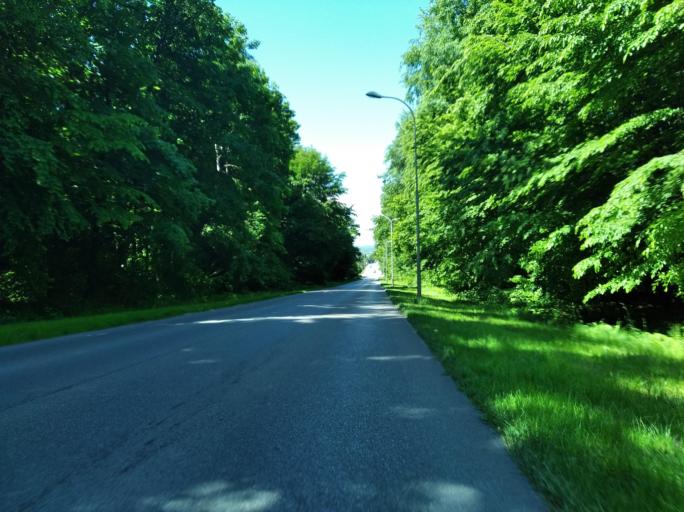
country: PL
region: Subcarpathian Voivodeship
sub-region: Powiat krosnienski
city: Jedlicze
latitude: 49.7242
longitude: 21.6650
